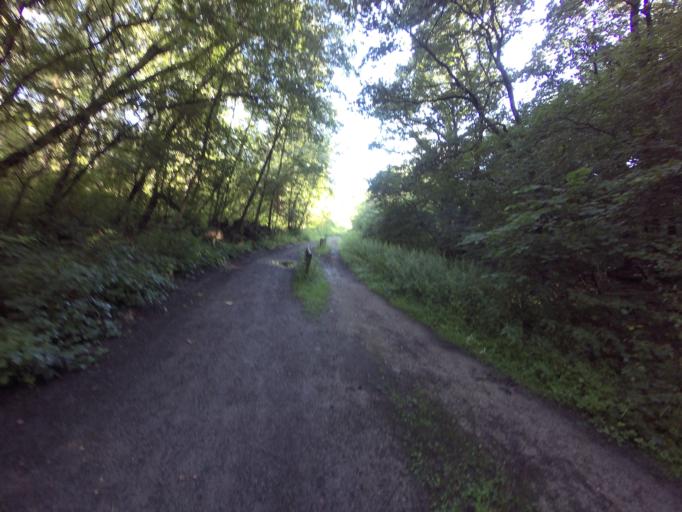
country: DE
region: North Rhine-Westphalia
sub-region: Regierungsbezirk Koln
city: Wurselen
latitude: 50.8265
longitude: 6.1116
